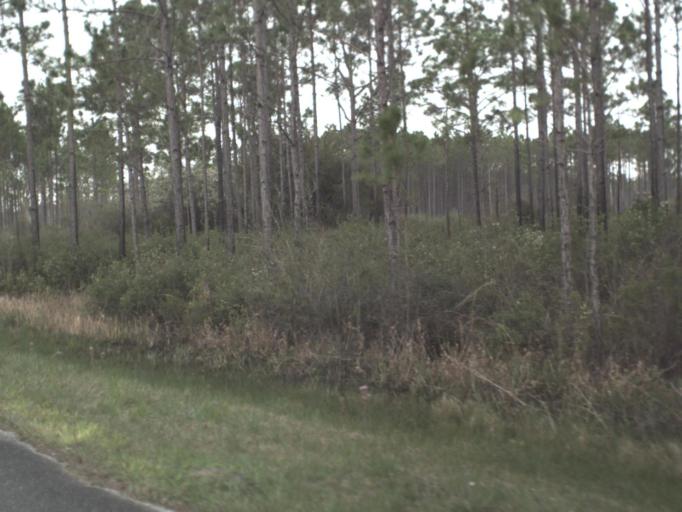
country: US
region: Florida
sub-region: Franklin County
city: Eastpoint
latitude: 29.8010
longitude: -84.8323
